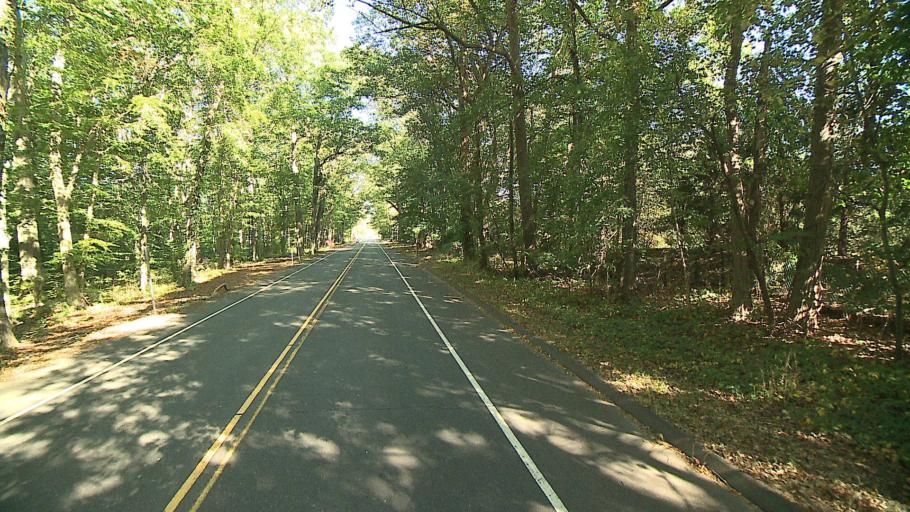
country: US
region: Connecticut
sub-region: Fairfield County
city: New Canaan
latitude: 41.1254
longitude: -73.4849
